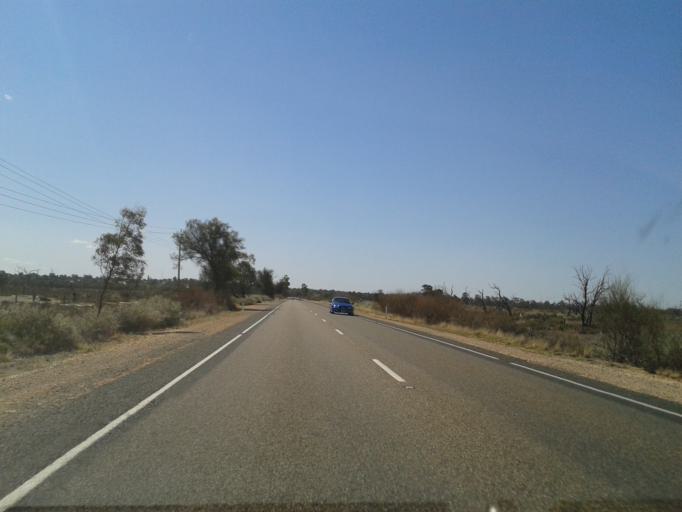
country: AU
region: South Australia
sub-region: Berri and Barmera
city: Berri
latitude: -34.3052
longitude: 140.6054
